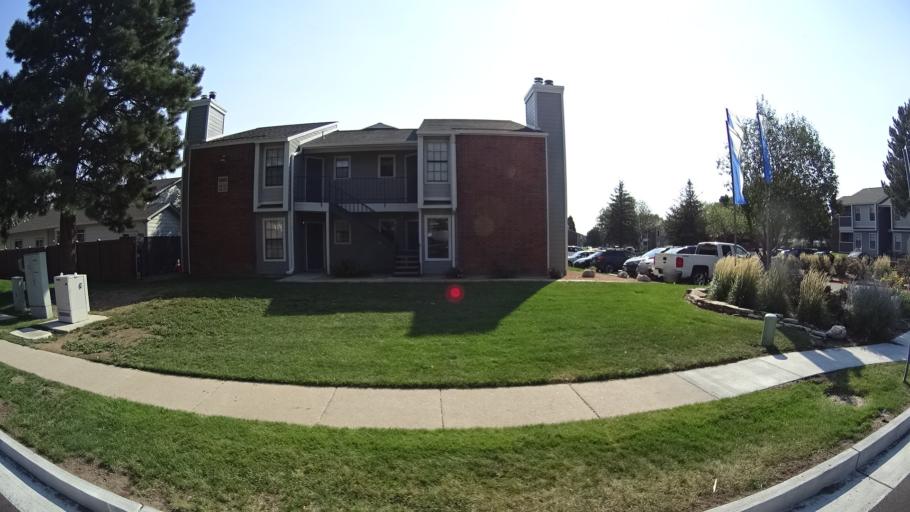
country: US
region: Colorado
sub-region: El Paso County
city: Stratmoor
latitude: 38.7737
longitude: -104.8109
